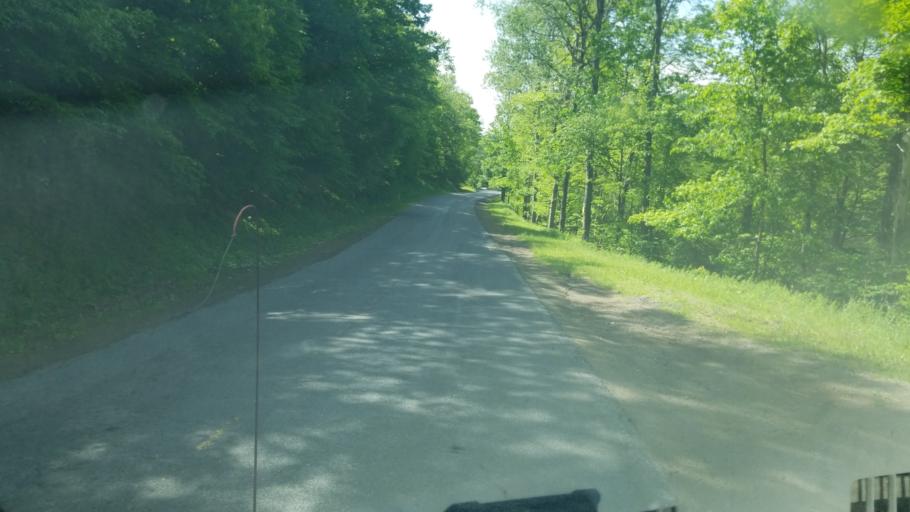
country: US
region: Pennsylvania
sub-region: Potter County
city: Galeton
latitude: 41.8545
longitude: -77.7090
